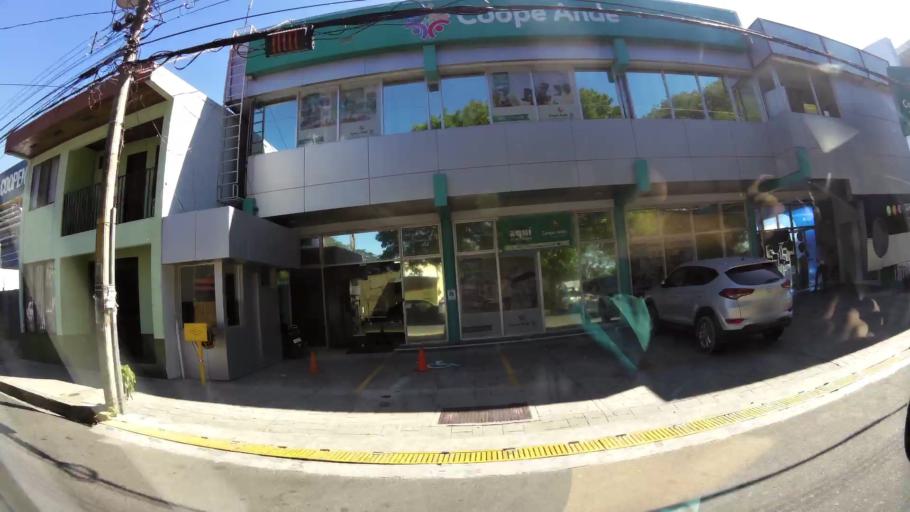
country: CR
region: Guanacaste
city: Liberia
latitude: 10.6292
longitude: -85.4402
